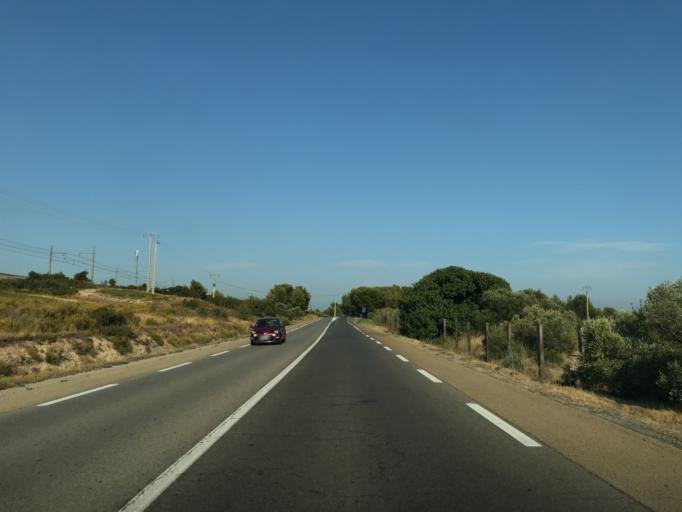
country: FR
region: Provence-Alpes-Cote d'Azur
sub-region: Departement des Bouches-du-Rhone
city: Cornillon-Confoux
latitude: 43.5277
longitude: 5.0899
